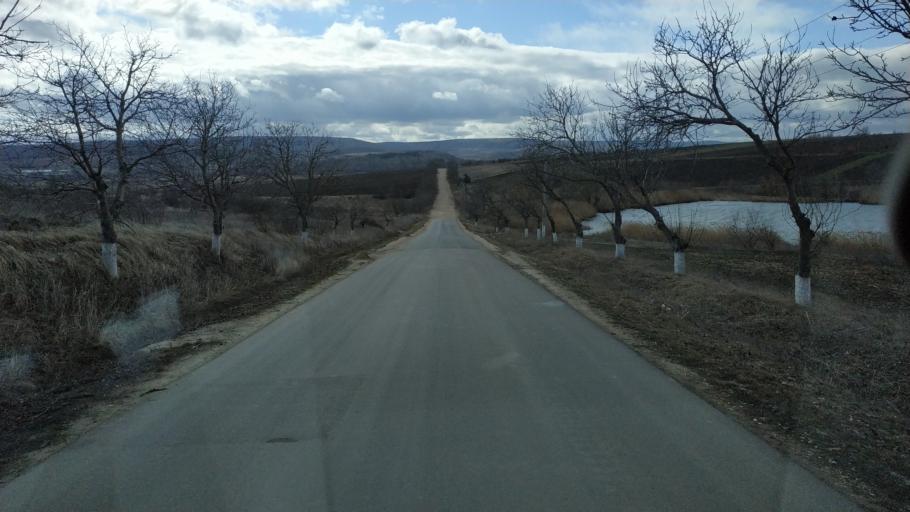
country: MD
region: Stinga Nistrului
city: Bucovat
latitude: 47.1992
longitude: 28.4907
